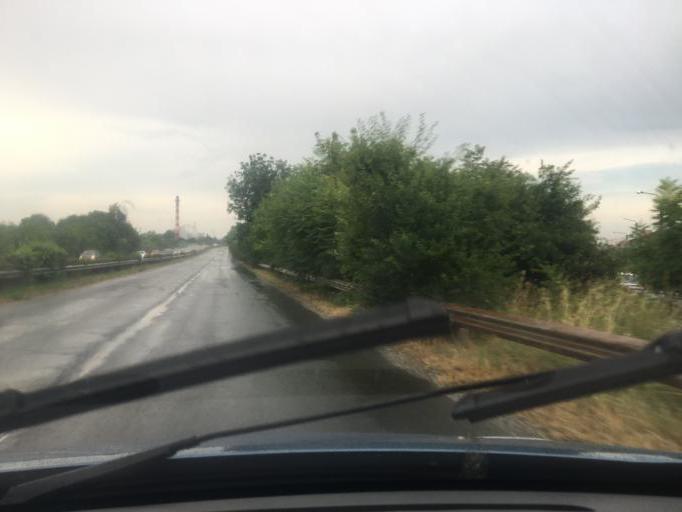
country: BG
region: Burgas
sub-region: Obshtina Burgas
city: Burgas
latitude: 42.5591
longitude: 27.5150
